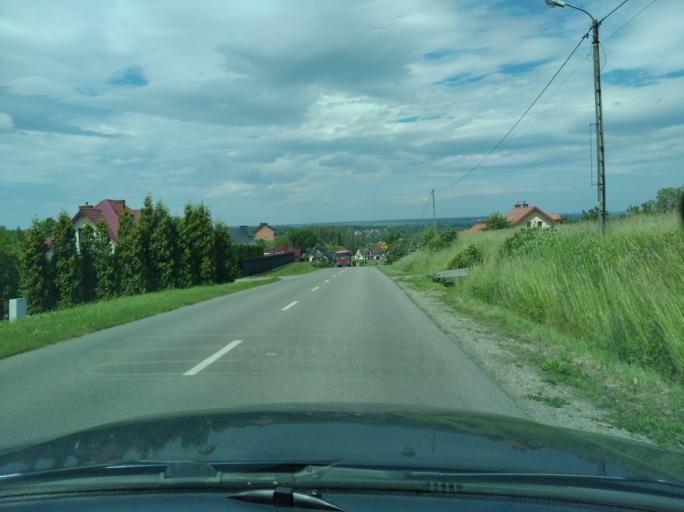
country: PL
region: Subcarpathian Voivodeship
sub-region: Powiat ropczycko-sedziszowski
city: Ropczyce
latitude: 50.0436
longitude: 21.6197
